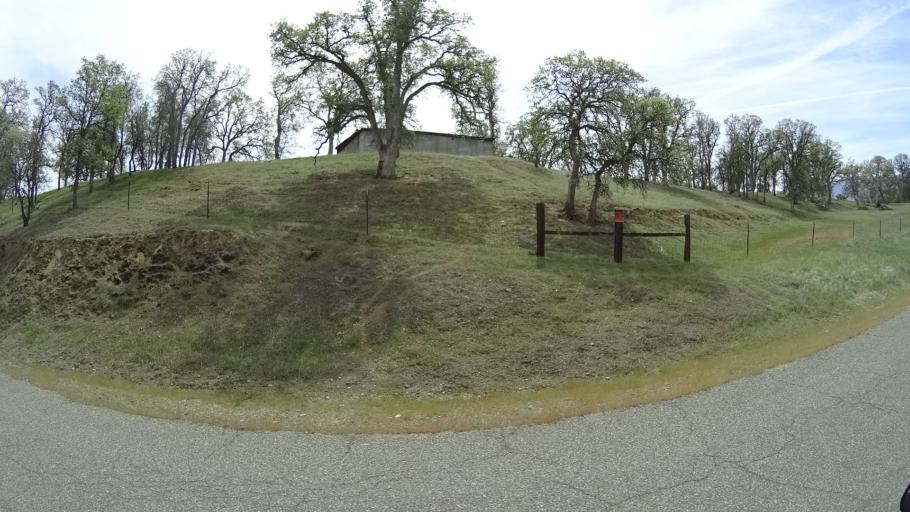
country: US
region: California
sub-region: Glenn County
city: Willows
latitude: 39.5951
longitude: -122.5497
